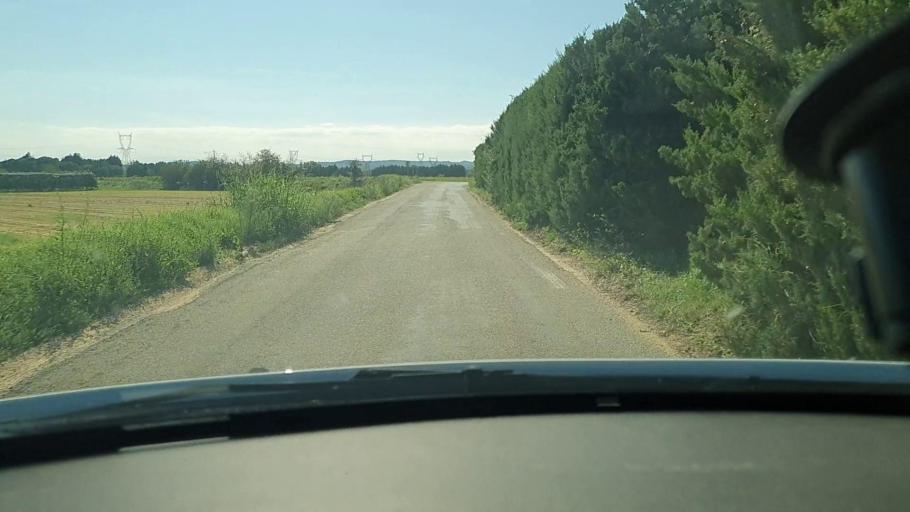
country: FR
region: Languedoc-Roussillon
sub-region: Departement du Gard
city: Saint-Julien-de-Peyrolas
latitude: 44.2872
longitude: 4.5713
